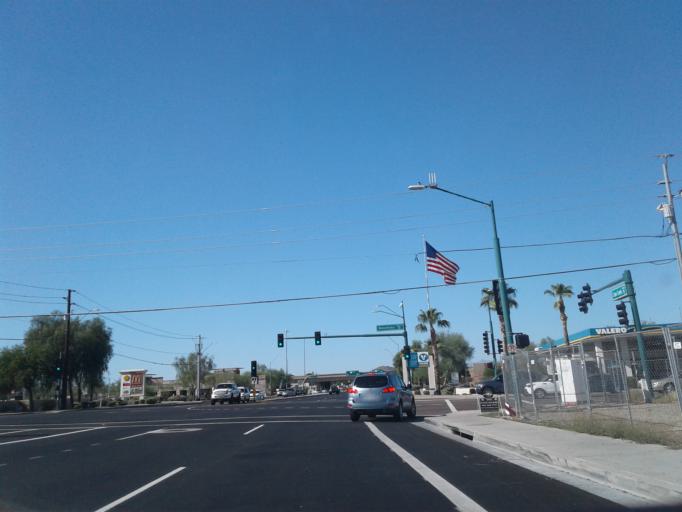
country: US
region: Arizona
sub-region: Maricopa County
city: Paradise Valley
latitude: 33.6690
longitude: -112.0306
